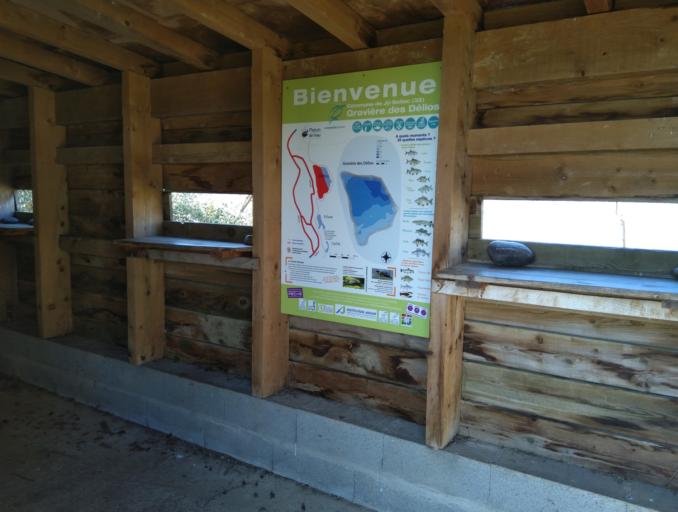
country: FR
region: Midi-Pyrenees
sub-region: Departement du Gers
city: Plaisance
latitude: 43.5712
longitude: 0.0035
